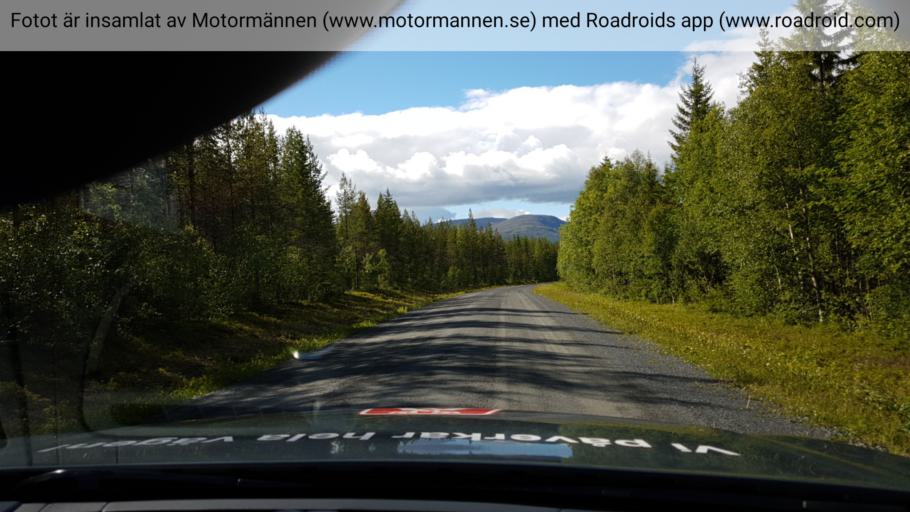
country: SE
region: Jaemtland
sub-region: Krokoms Kommun
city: Valla
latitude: 63.0853
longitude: 13.9169
